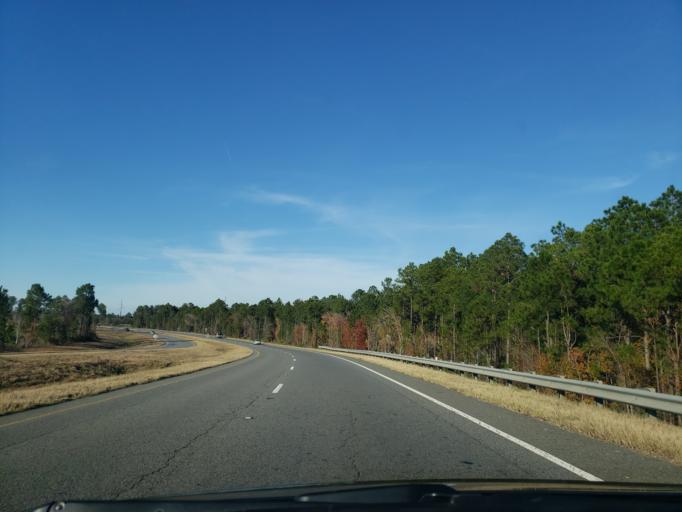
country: US
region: Georgia
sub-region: Ware County
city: Deenwood
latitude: 31.2362
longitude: -82.4267
